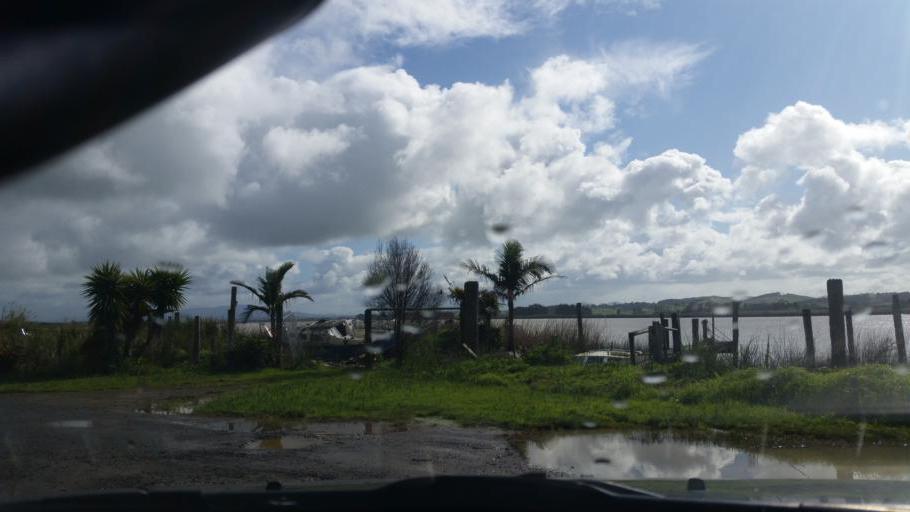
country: NZ
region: Northland
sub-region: Kaipara District
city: Dargaville
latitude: -36.0258
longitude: 173.9199
